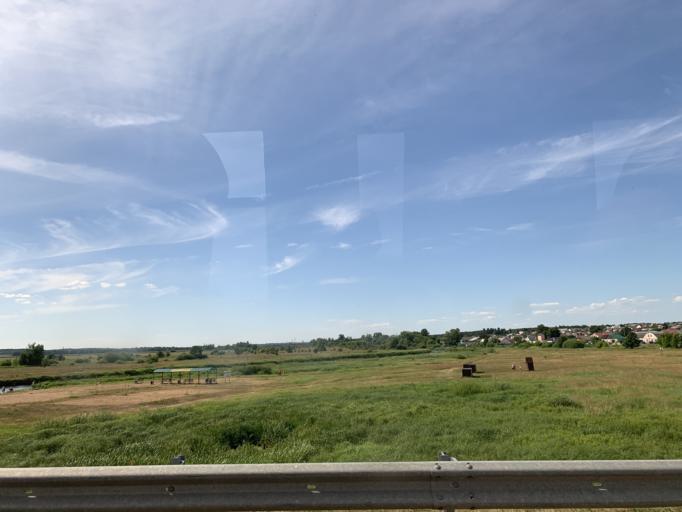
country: BY
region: Minsk
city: Stowbtsy
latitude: 53.4707
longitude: 26.7301
